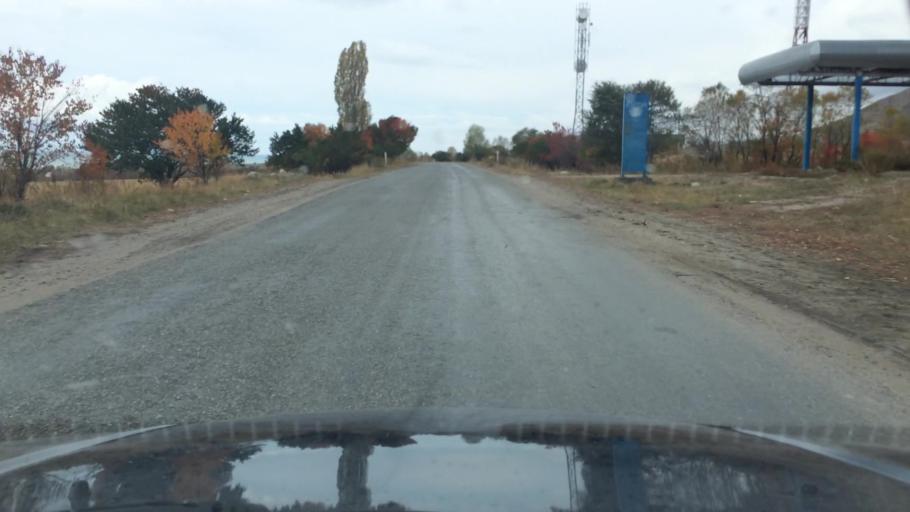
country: KG
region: Ysyk-Koel
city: Tyup
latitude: 42.7356
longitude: 77.9803
